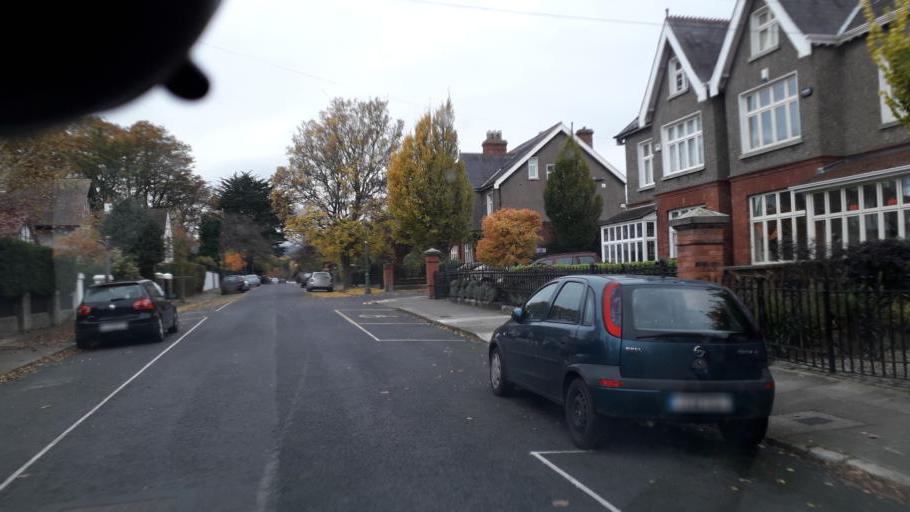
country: IE
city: Milltown
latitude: 53.3179
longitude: -6.2514
